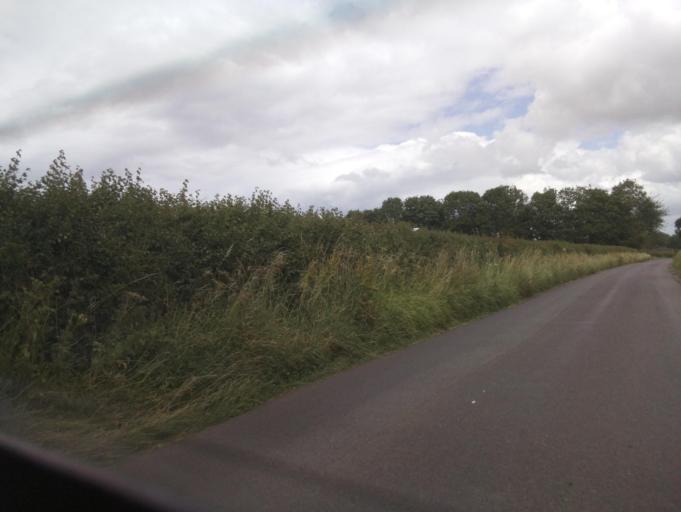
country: GB
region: England
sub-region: Wiltshire
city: Malmesbury
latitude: 51.5403
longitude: -2.0672
